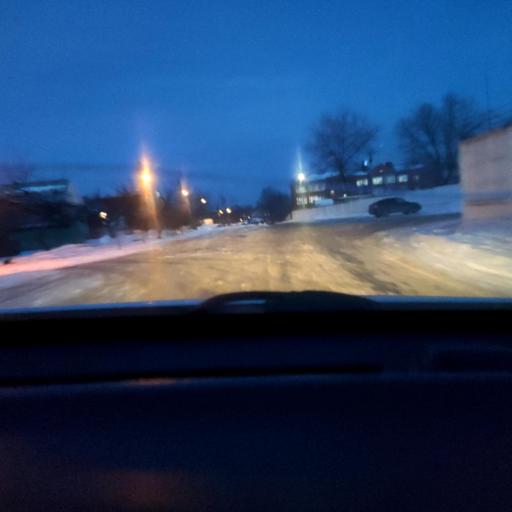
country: RU
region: Voronezj
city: Maslovka
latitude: 51.6088
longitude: 39.2296
